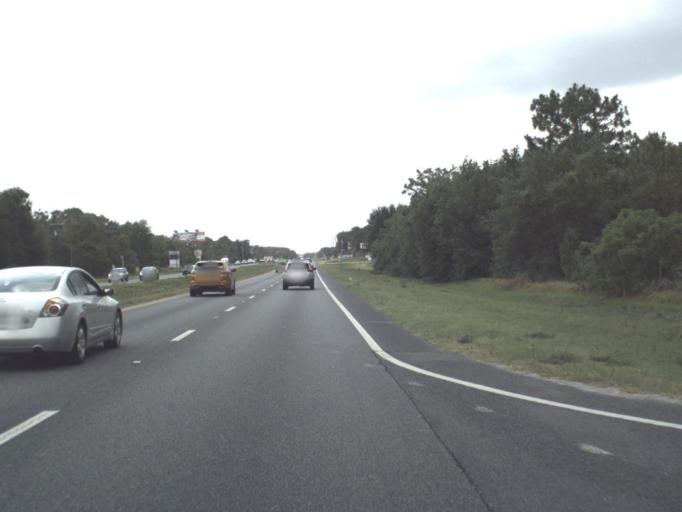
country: US
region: Florida
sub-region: Sumter County
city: The Villages
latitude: 29.0006
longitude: -82.0012
